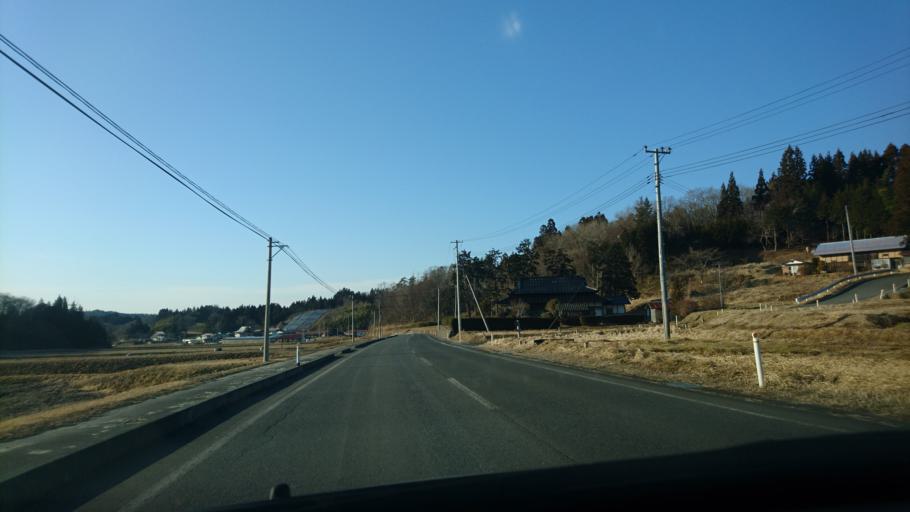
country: JP
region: Iwate
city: Ichinoseki
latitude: 38.8980
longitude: 141.3918
